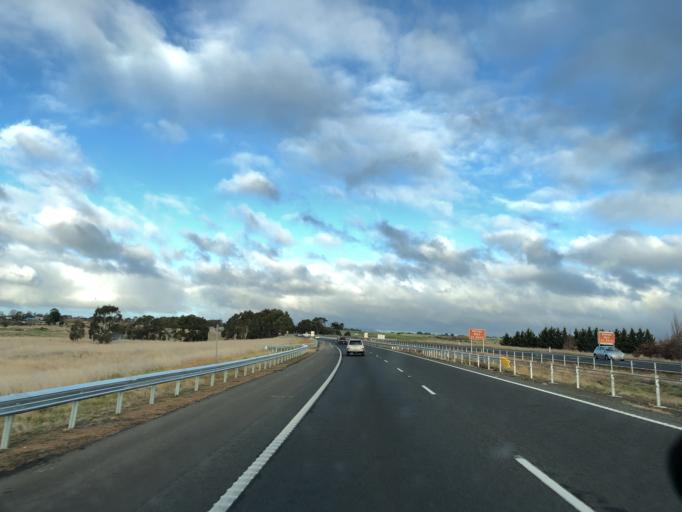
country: AU
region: Victoria
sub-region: Mount Alexander
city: Castlemaine
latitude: -37.2204
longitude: 144.4172
